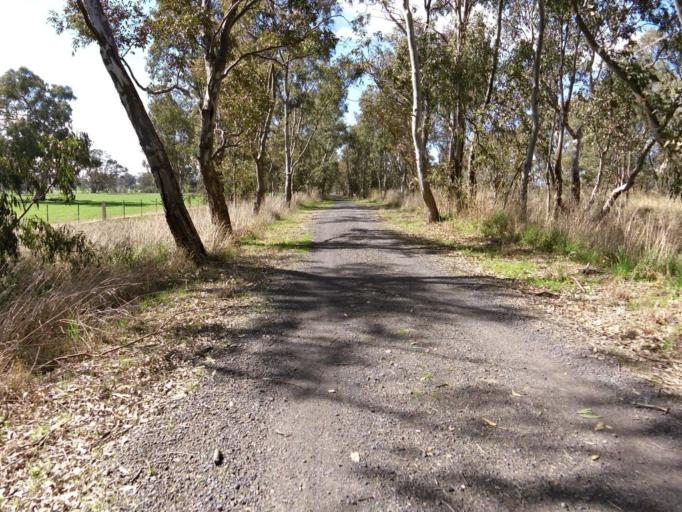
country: AU
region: Victoria
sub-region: Mansfield
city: Mansfield
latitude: -37.0456
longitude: 146.0511
